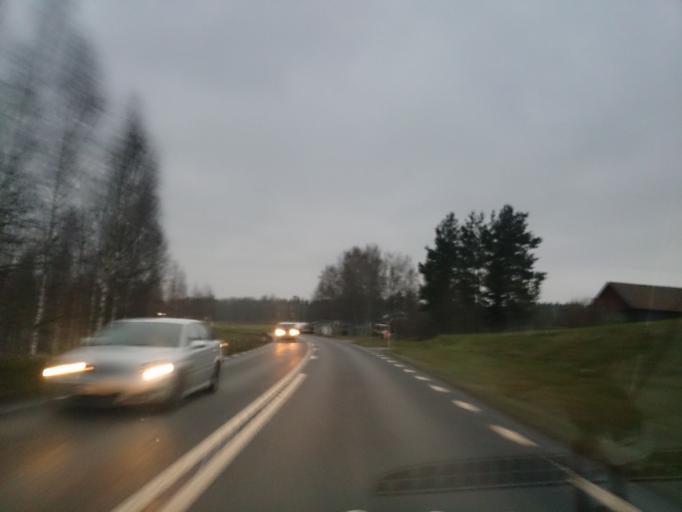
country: SE
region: OEstergoetland
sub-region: Linkopings Kommun
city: Sturefors
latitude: 58.3243
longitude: 15.8606
